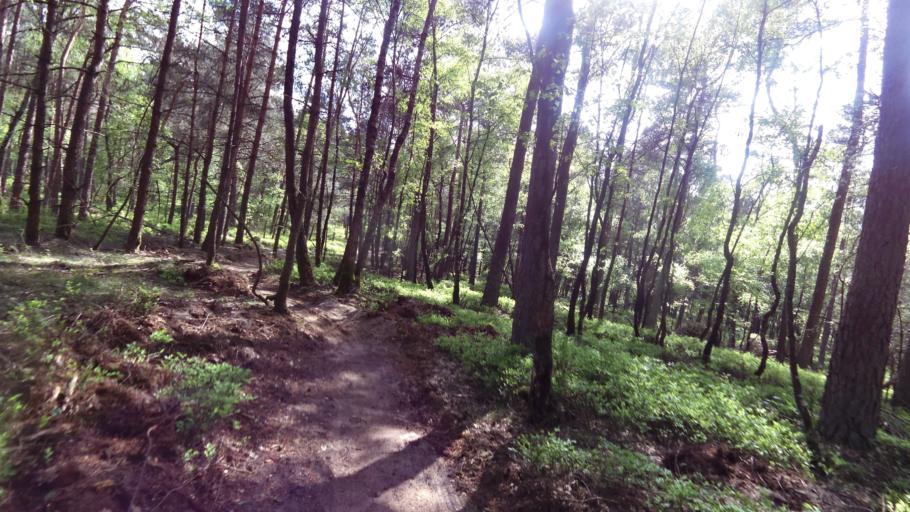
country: NL
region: Gelderland
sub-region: Gemeente Brummen
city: Eerbeek
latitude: 52.0760
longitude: 6.0394
